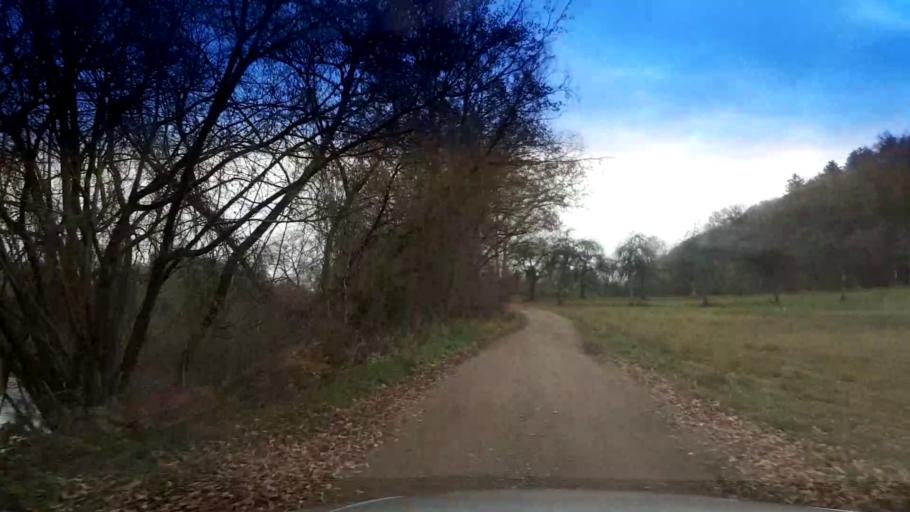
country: DE
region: Bavaria
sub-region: Upper Franconia
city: Kemmern
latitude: 49.9573
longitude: 10.8603
